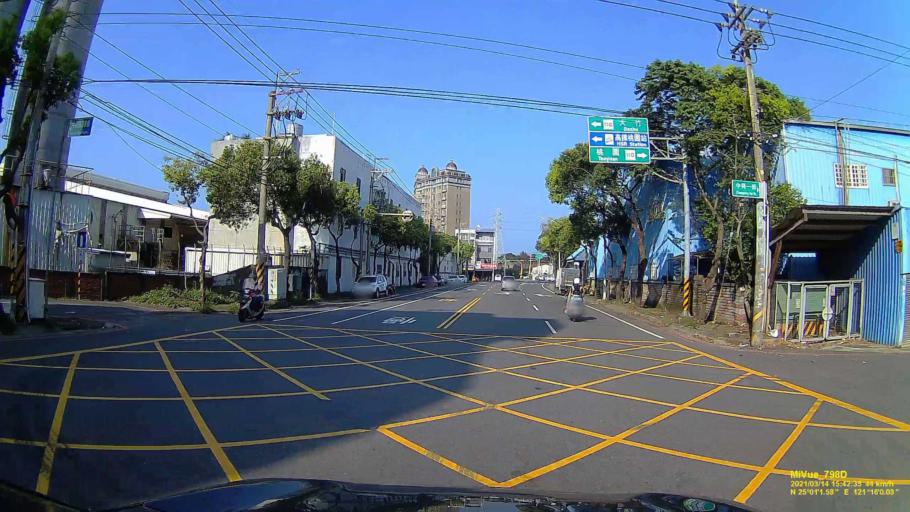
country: TW
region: Taiwan
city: Taoyuan City
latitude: 25.0173
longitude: 121.2669
